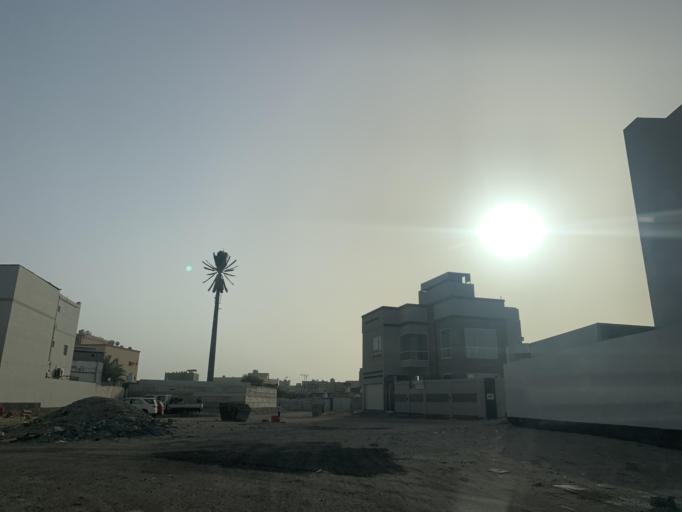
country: BH
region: Northern
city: Madinat `Isa
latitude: 26.1623
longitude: 50.5136
